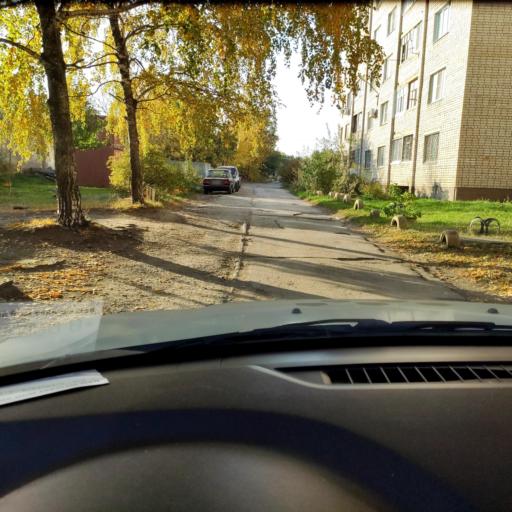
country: RU
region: Samara
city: Tol'yatti
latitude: 53.5390
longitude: 49.4031
